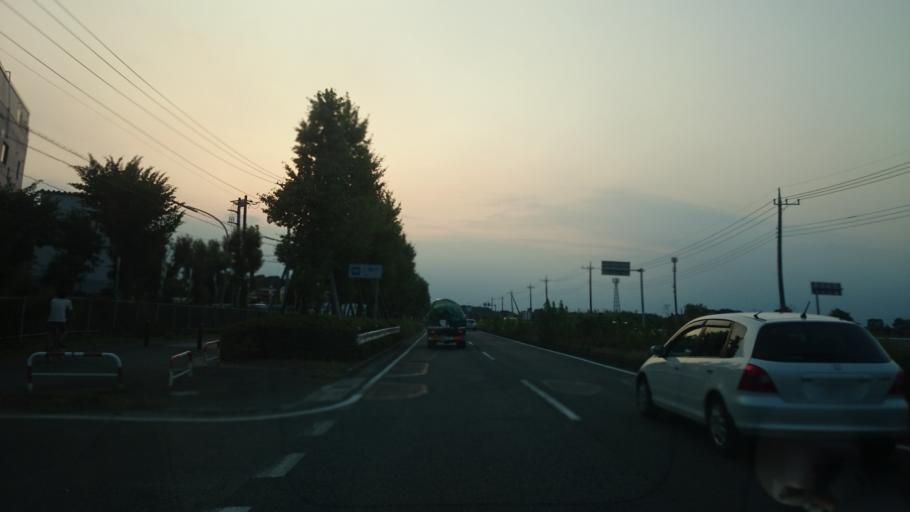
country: JP
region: Saitama
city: Hasuda
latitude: 35.9608
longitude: 139.6502
